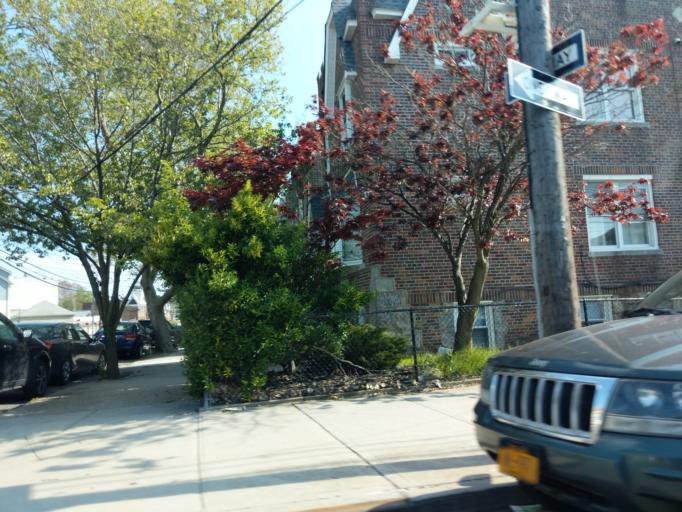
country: US
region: New York
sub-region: Queens County
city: Long Island City
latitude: 40.7290
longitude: -73.8947
